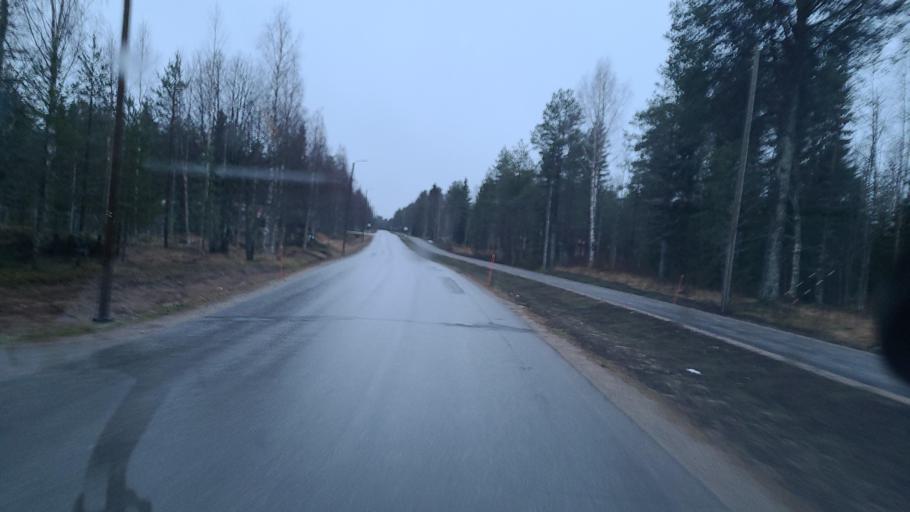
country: FI
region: Lapland
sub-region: Rovaniemi
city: Ranua
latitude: 65.9307
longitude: 26.4975
